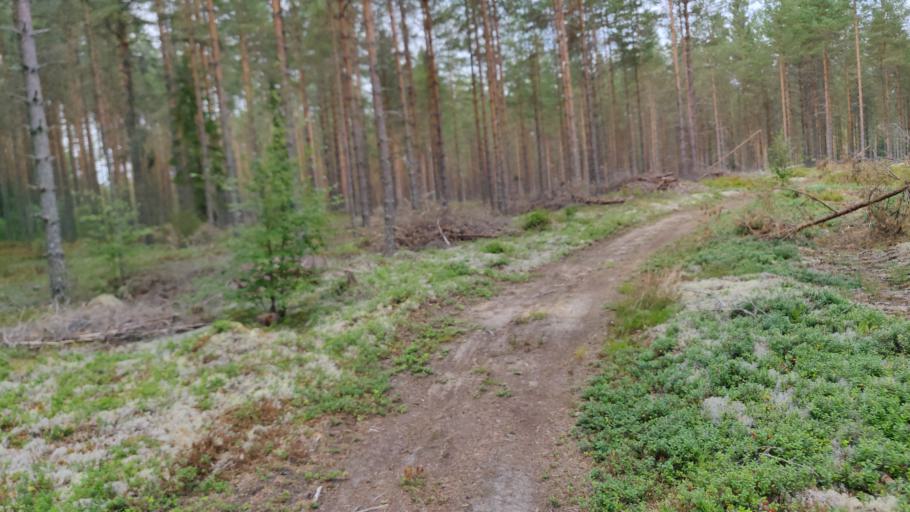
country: SE
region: Vaermland
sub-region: Hagfors Kommun
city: Hagfors
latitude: 60.0281
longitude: 13.5429
